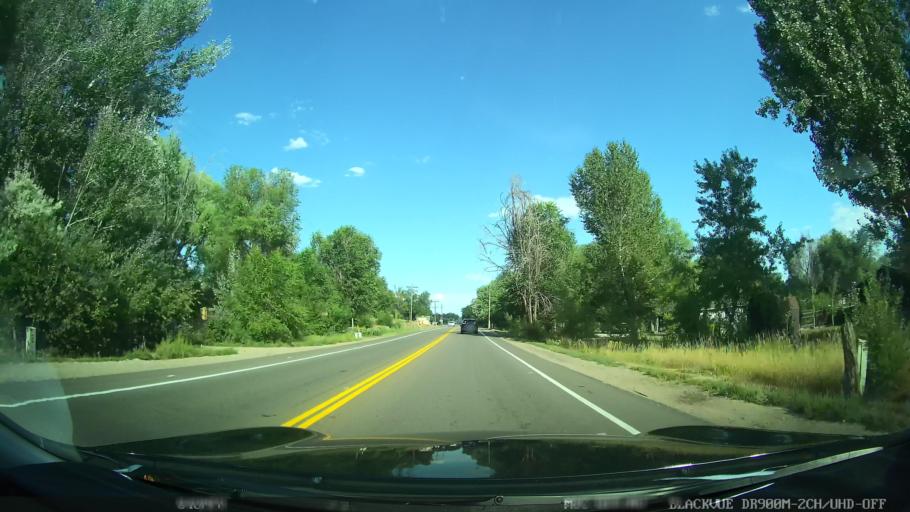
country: US
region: Colorado
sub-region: Larimer County
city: Loveland
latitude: 40.4073
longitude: -105.1380
